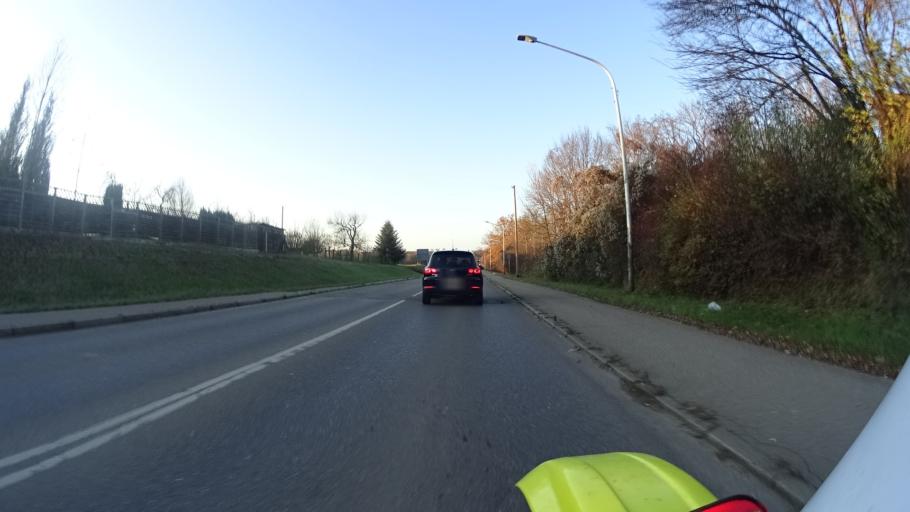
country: DE
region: Baden-Wuerttemberg
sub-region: Regierungsbezirk Stuttgart
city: Schlat
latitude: 48.6716
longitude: 9.6911
